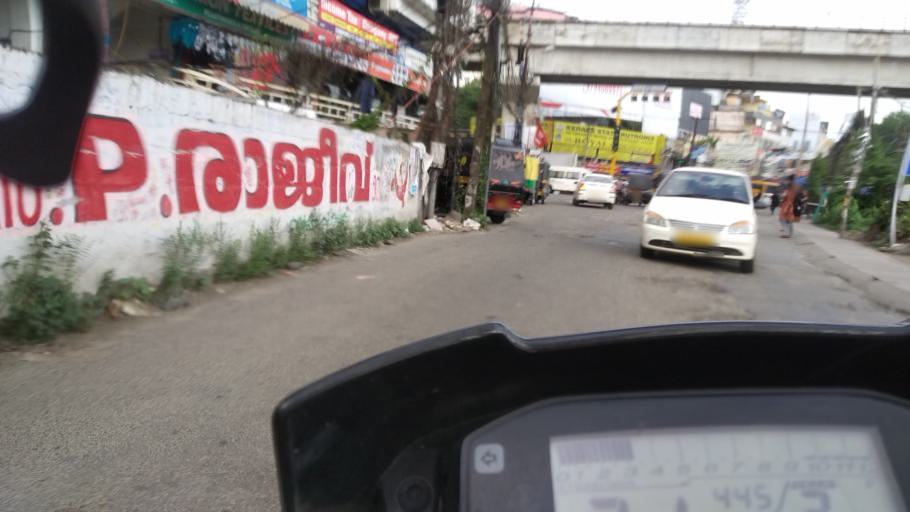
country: IN
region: Kerala
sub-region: Ernakulam
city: Cochin
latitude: 9.9955
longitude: 76.2918
